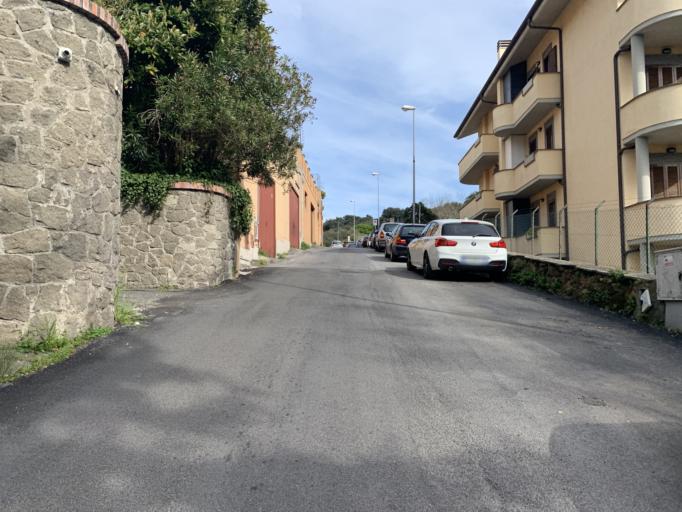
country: IT
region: Latium
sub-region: Citta metropolitana di Roma Capitale
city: Grottaferrata
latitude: 41.7679
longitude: 12.6652
